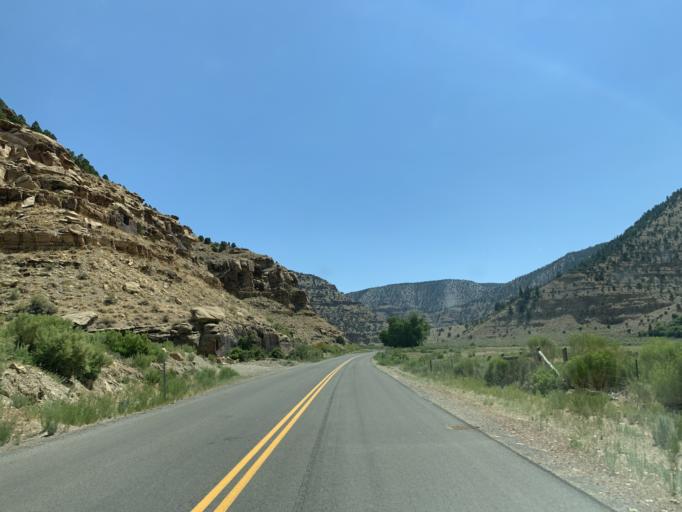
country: US
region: Utah
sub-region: Carbon County
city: East Carbon City
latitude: 39.8011
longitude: -110.3647
